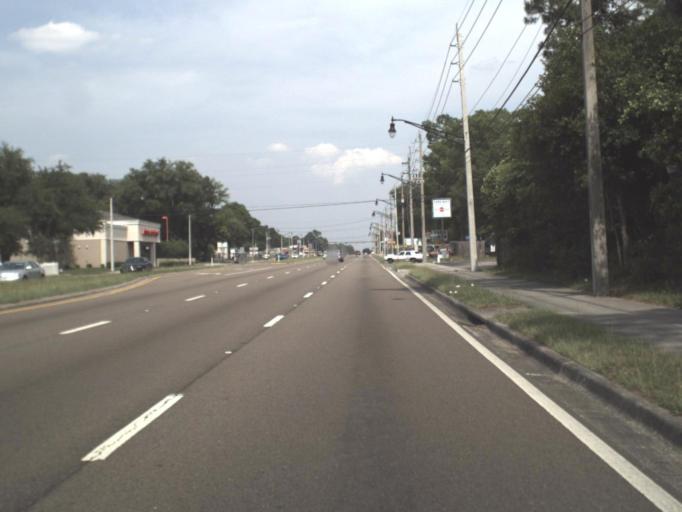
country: US
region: Florida
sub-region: Clay County
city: Bellair-Meadowbrook Terrace
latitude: 30.2478
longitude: -81.7909
